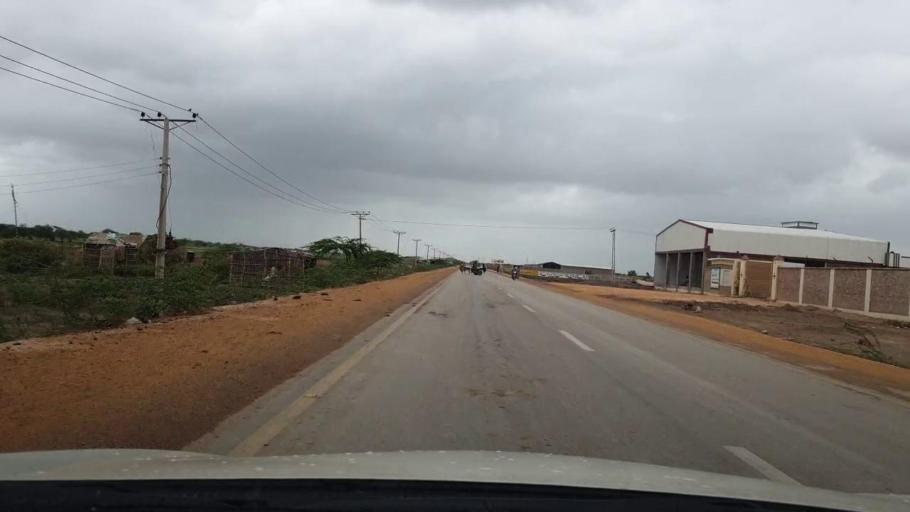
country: PK
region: Sindh
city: Badin
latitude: 24.6537
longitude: 68.7658
